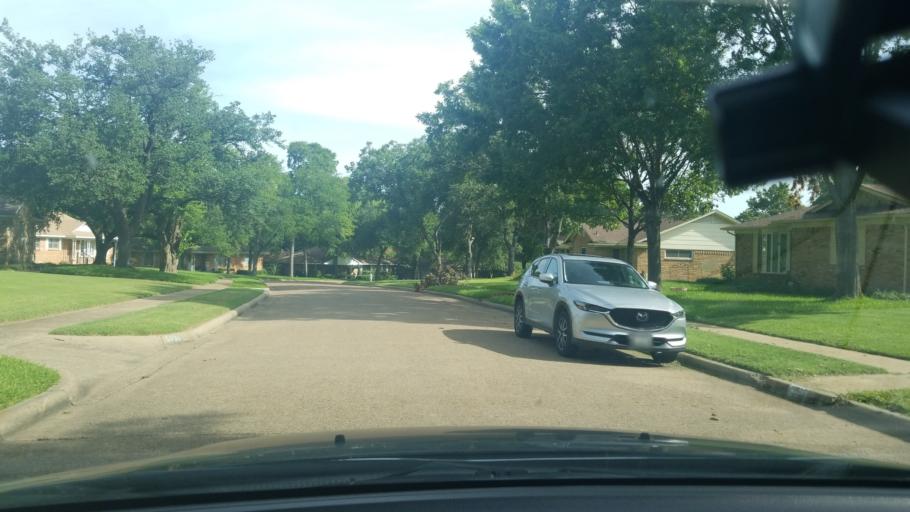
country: US
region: Texas
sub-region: Dallas County
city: Highland Park
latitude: 32.7976
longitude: -96.7029
